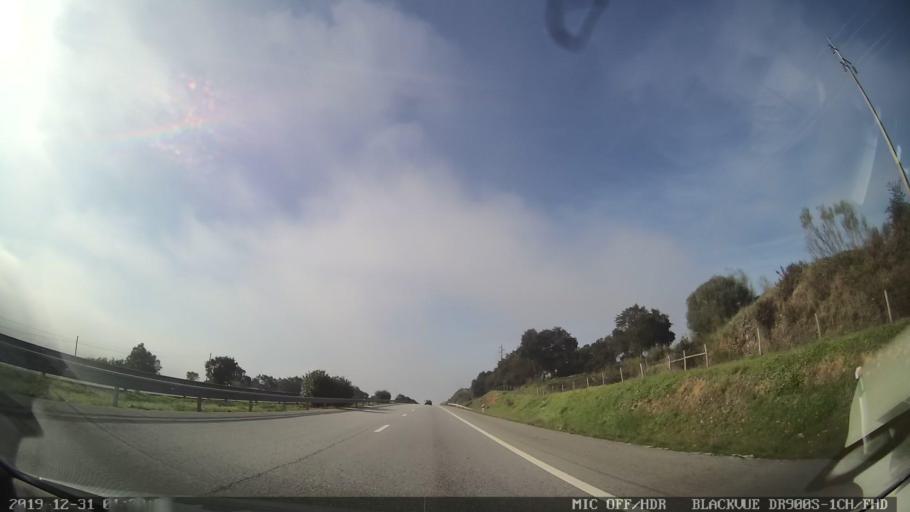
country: PT
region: Santarem
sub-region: Abrantes
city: Alferrarede
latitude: 39.4858
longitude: -8.1352
